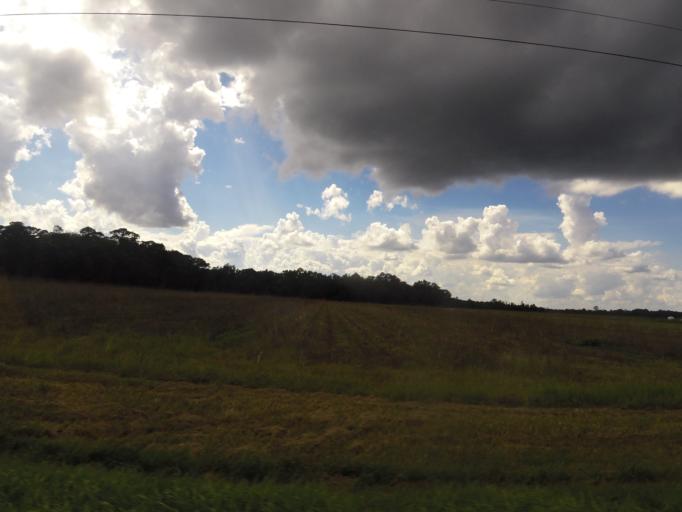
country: US
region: Florida
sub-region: Putnam County
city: East Palatka
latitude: 29.7502
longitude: -81.4757
